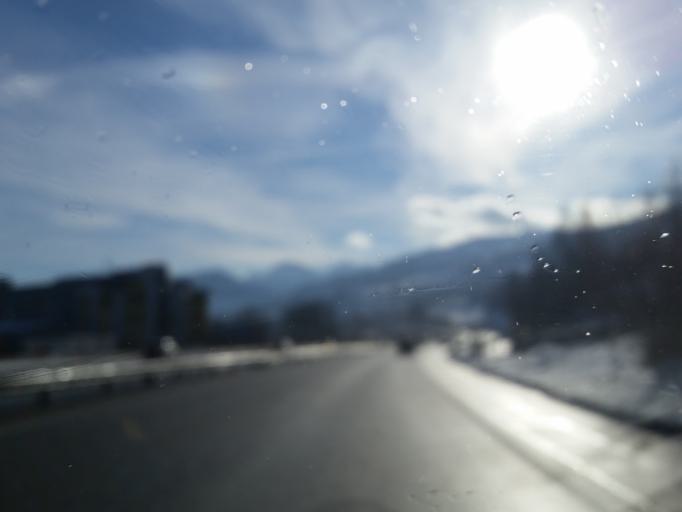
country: CH
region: Schwyz
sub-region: Bezirk March
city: Altendorf
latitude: 47.1986
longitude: 8.8105
